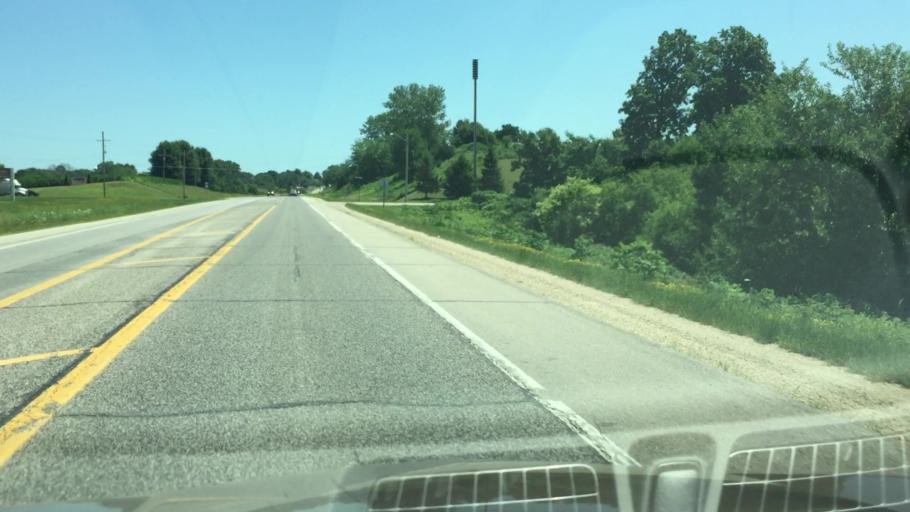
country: US
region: Iowa
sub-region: Linn County
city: Mount Vernon
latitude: 41.9172
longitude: -91.4025
